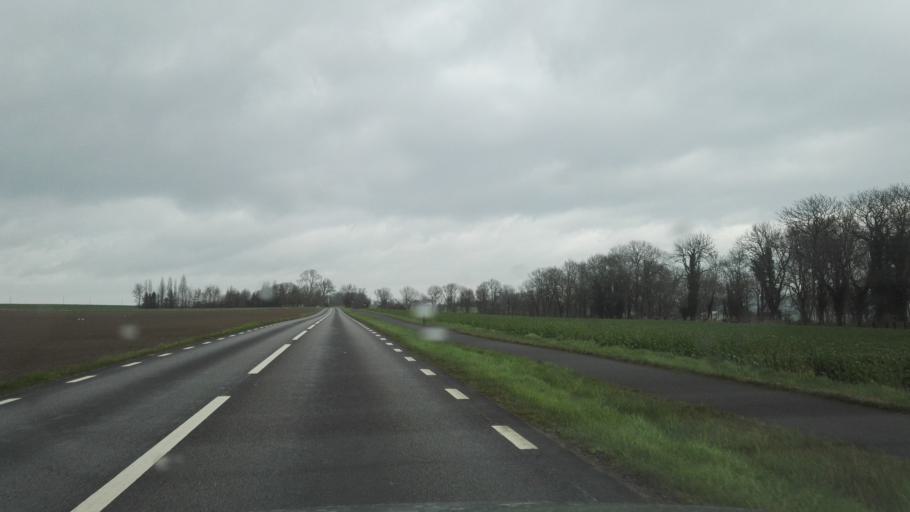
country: SE
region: Skane
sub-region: Simrishamns Kommun
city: Simrishamn
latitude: 55.5018
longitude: 14.3244
